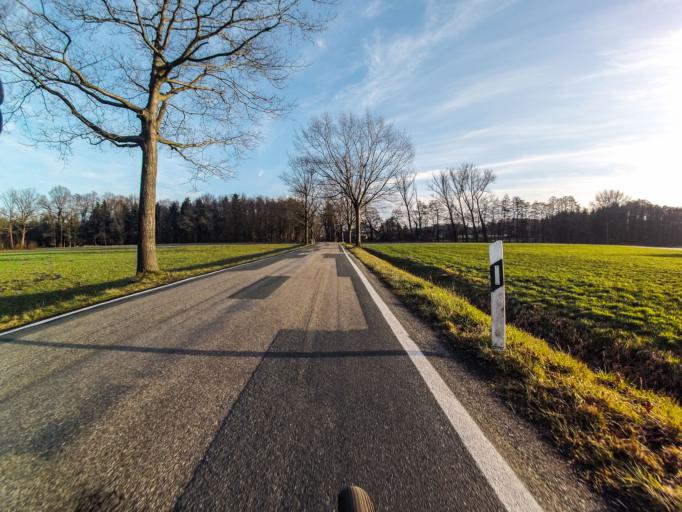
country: DE
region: North Rhine-Westphalia
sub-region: Regierungsbezirk Munster
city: Mettingen
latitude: 52.2992
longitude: 7.8203
